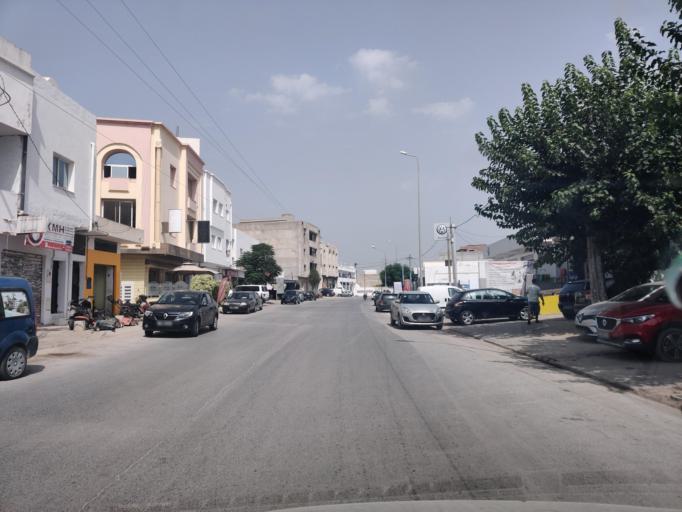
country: TN
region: Nabul
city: Al Hammamat
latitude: 36.4120
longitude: 10.5987
